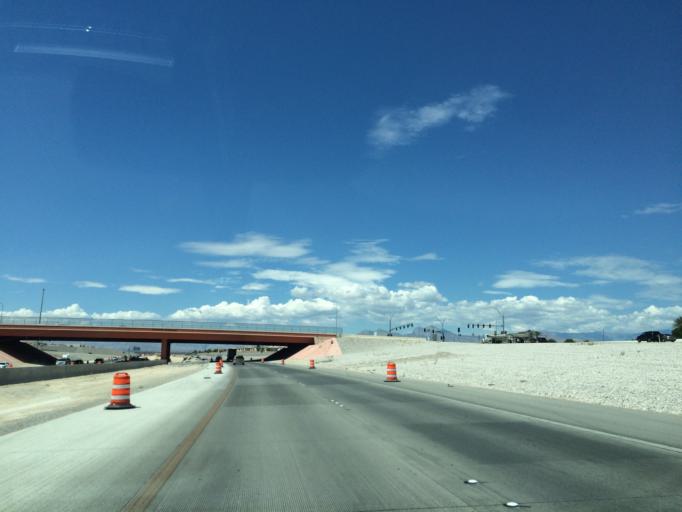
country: US
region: Nevada
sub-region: Clark County
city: North Las Vegas
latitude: 36.2911
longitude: -115.1786
